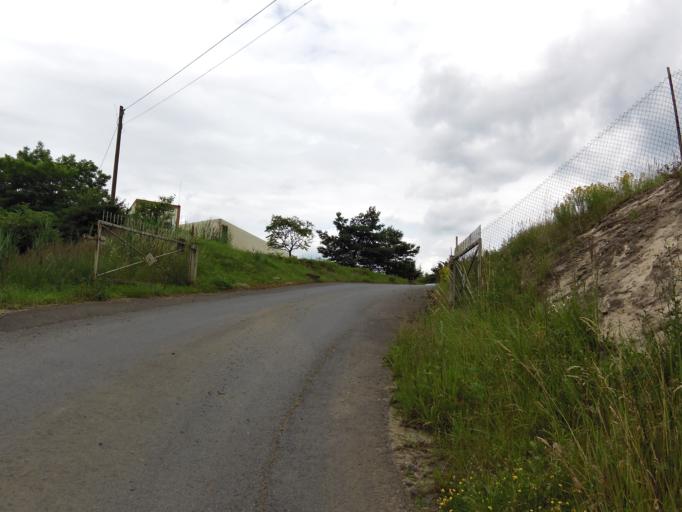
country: DE
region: Thuringia
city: Tiefenort
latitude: 50.8230
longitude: 10.1329
